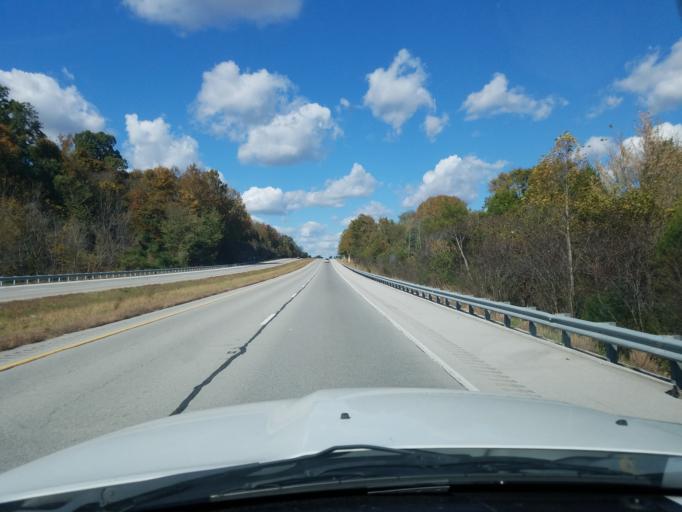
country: US
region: Kentucky
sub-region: Butler County
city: Morgantown
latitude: 37.0721
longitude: -86.6085
